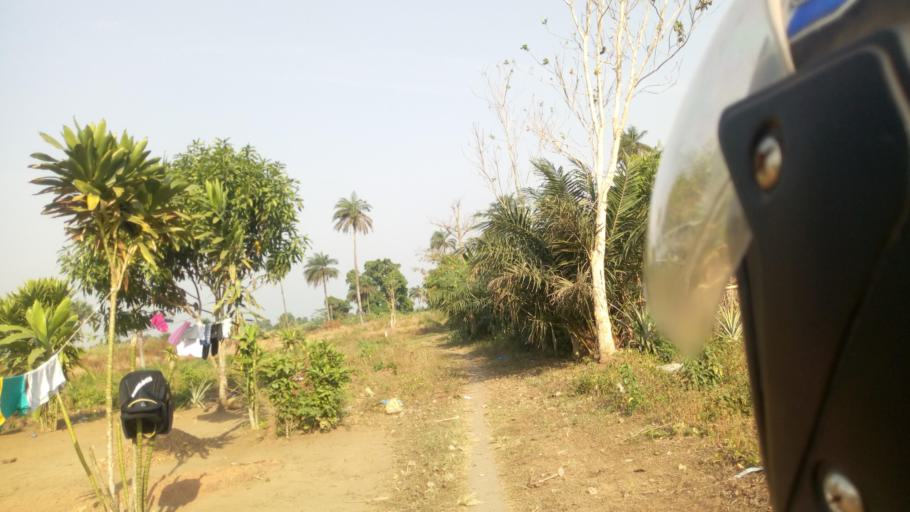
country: SL
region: Southern Province
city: Mogbwemo
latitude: 7.6151
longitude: -12.1738
